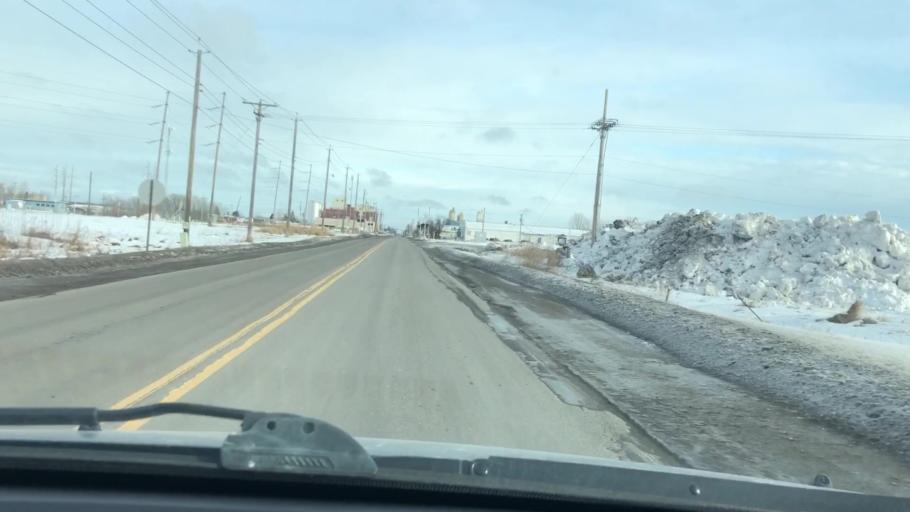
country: US
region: Wisconsin
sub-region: Douglas County
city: Superior
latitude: 46.7279
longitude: -92.1139
